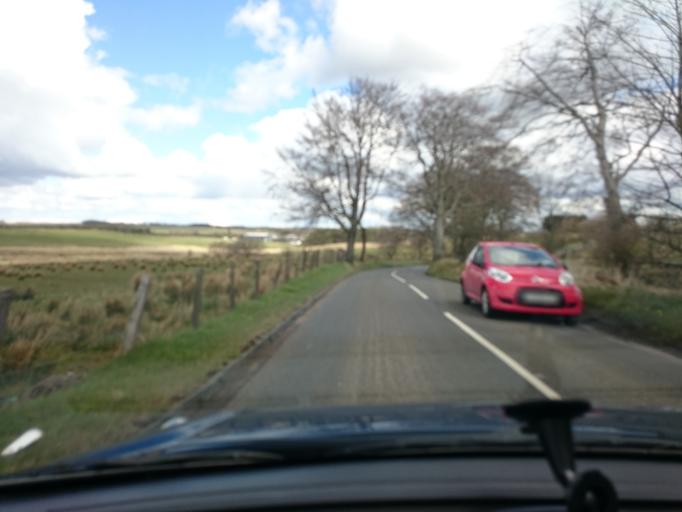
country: GB
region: Scotland
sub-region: Falkirk
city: Slamannan
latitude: 55.9329
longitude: -3.8522
